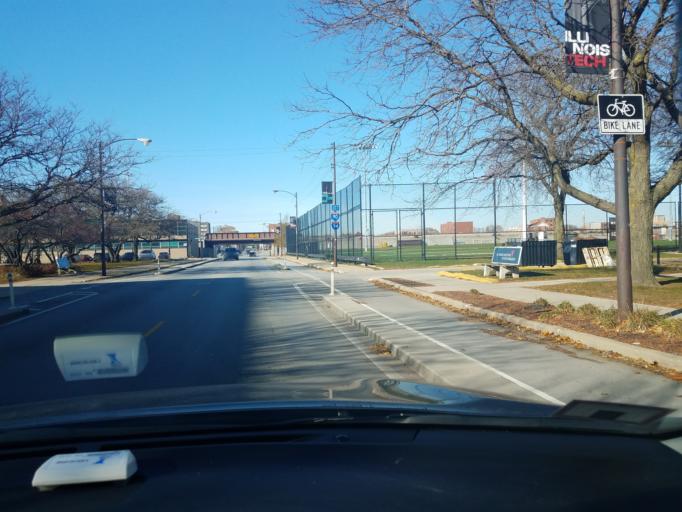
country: US
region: Illinois
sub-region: Cook County
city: Chicago
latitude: 41.8383
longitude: -87.6276
